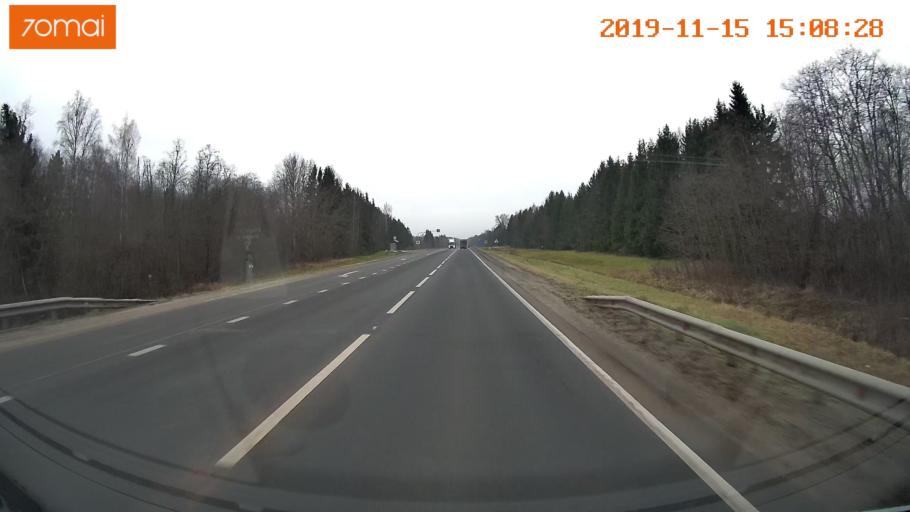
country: RU
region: Jaroslavl
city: Prechistoye
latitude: 58.3706
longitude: 40.2765
